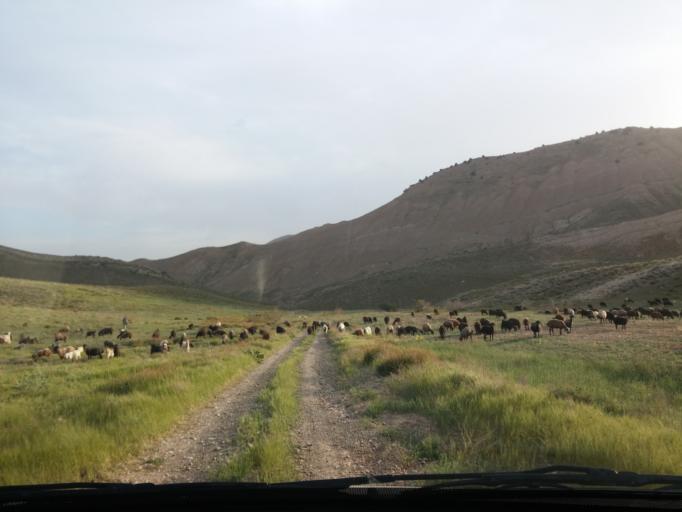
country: IR
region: Semnan
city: Istgah-e Rah Ahan-e Garmsar
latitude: 35.4871
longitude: 52.2965
